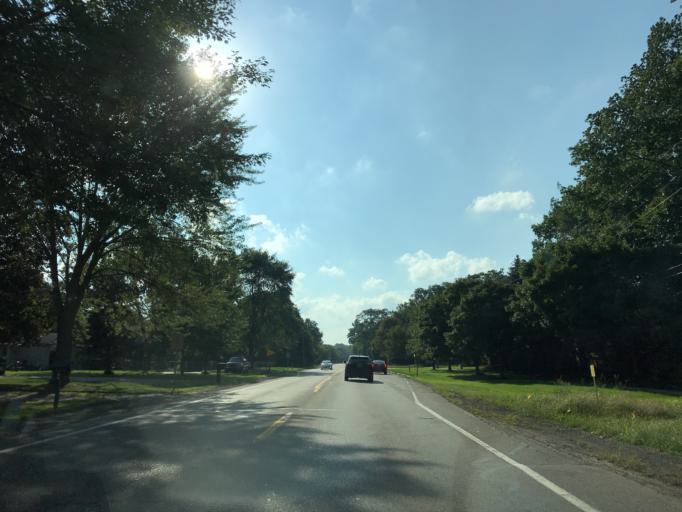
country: US
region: Michigan
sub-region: Wayne County
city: Plymouth
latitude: 42.3955
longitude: -83.4532
